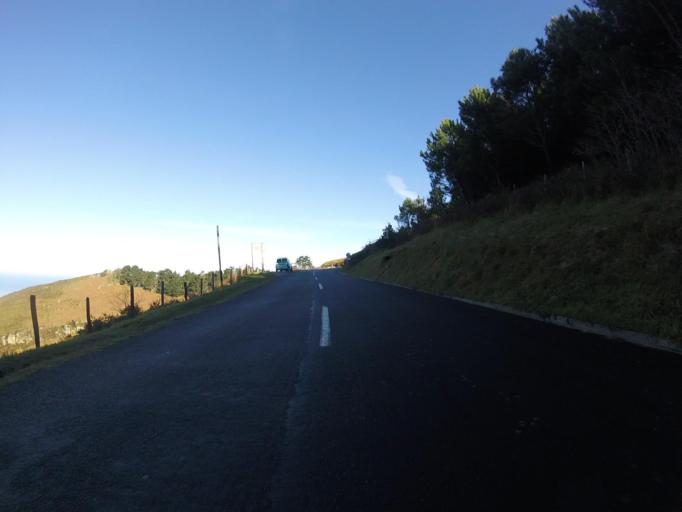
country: ES
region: Basque Country
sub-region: Provincia de Guipuzcoa
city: Lezo
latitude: 43.3427
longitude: -1.8645
